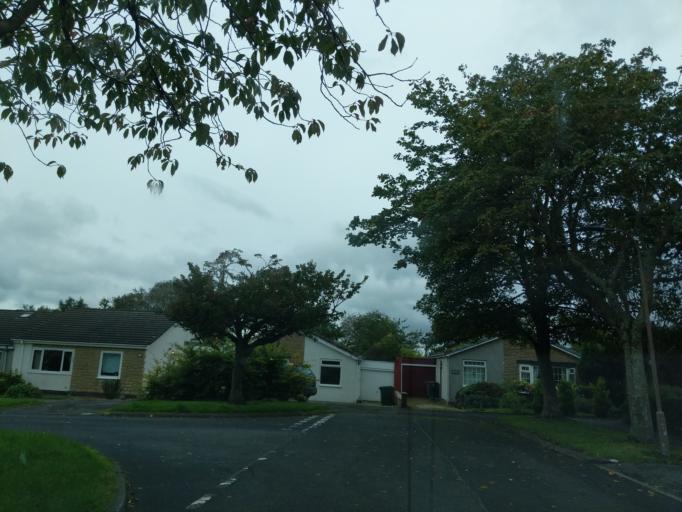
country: GB
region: Scotland
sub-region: Edinburgh
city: Balerno
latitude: 55.8783
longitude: -3.3454
